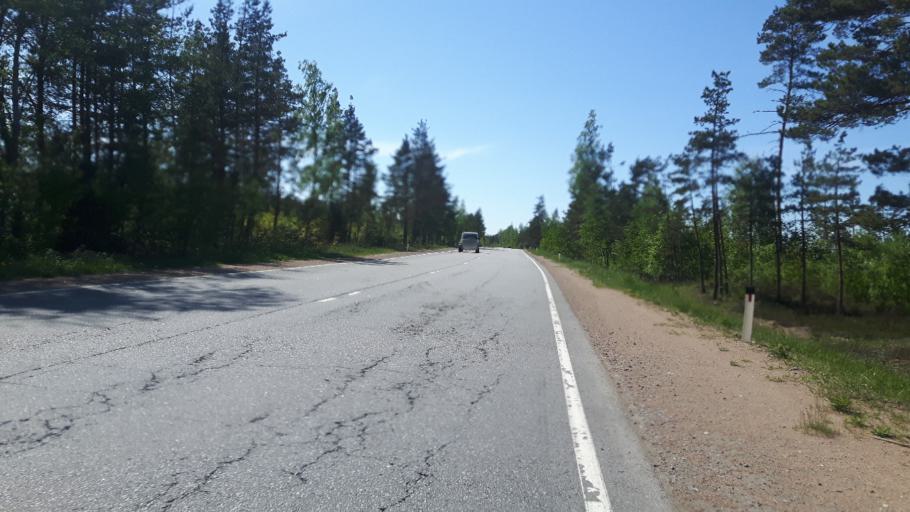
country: RU
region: Leningrad
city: Sista-Palkino
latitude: 59.7695
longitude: 28.7880
